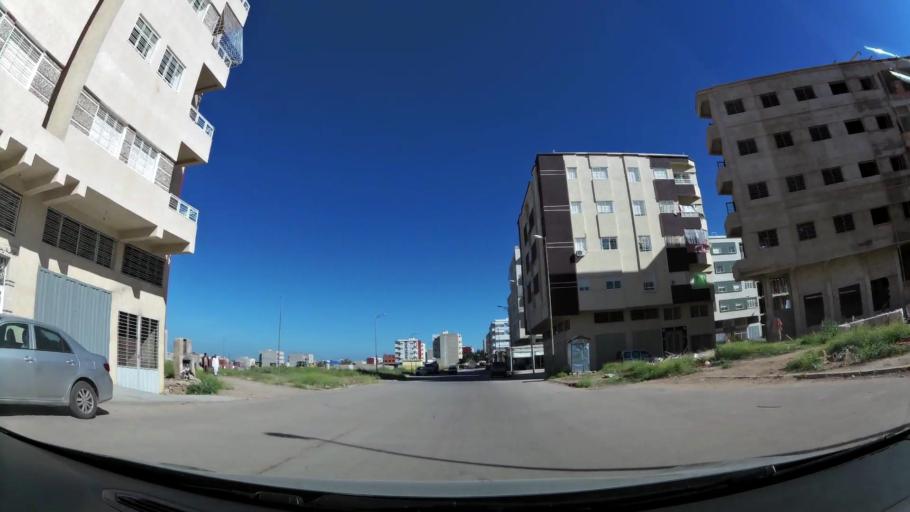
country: MA
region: Fes-Boulemane
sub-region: Fes
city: Fes
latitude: 34.0145
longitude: -4.9623
